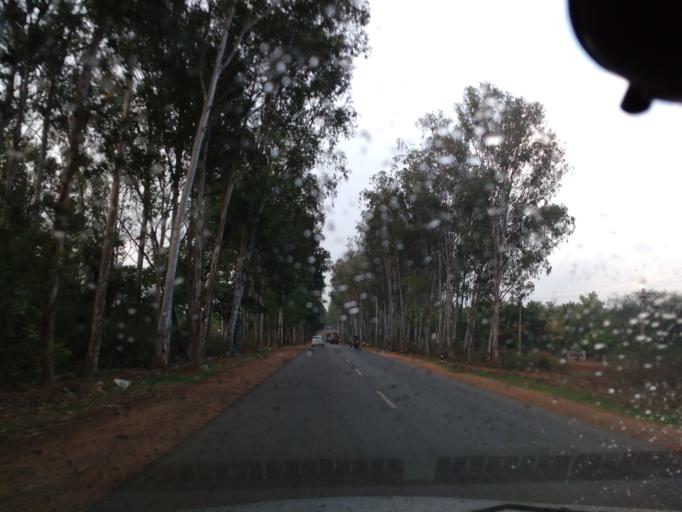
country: IN
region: Karnataka
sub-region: Tumkur
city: Tiptur
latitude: 13.2638
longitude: 76.4964
